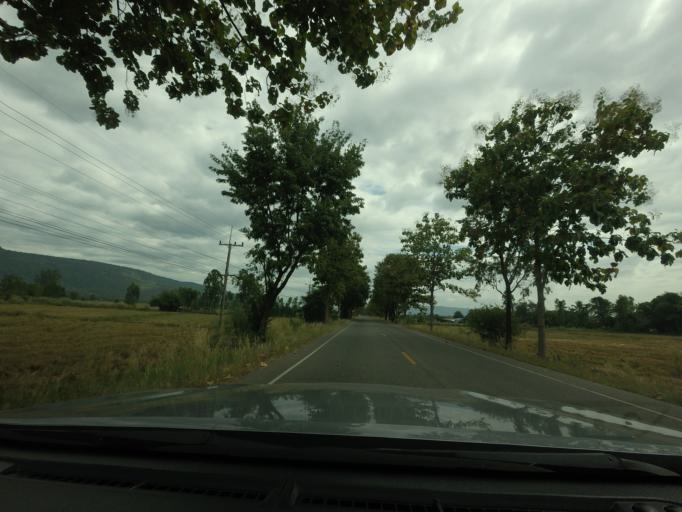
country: TH
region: Phitsanulok
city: Wang Thong
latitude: 16.7088
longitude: 100.4867
